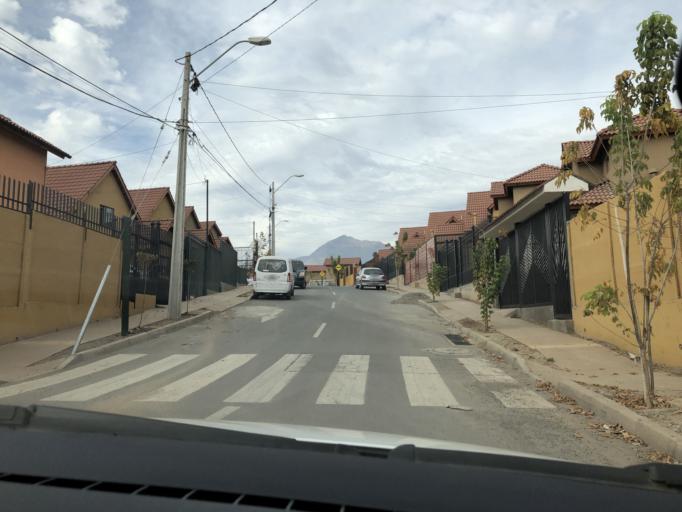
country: CL
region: Santiago Metropolitan
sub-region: Provincia de Cordillera
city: Puente Alto
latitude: -33.5861
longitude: -70.5316
